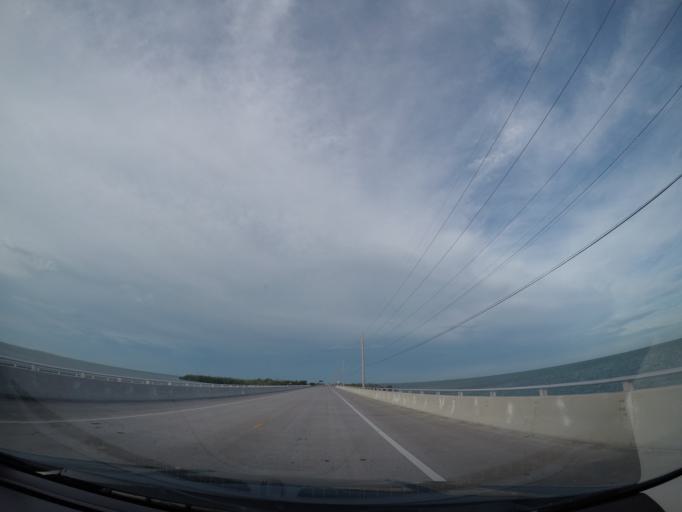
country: US
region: Florida
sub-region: Monroe County
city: Big Pine Key
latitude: 24.6749
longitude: -81.2413
